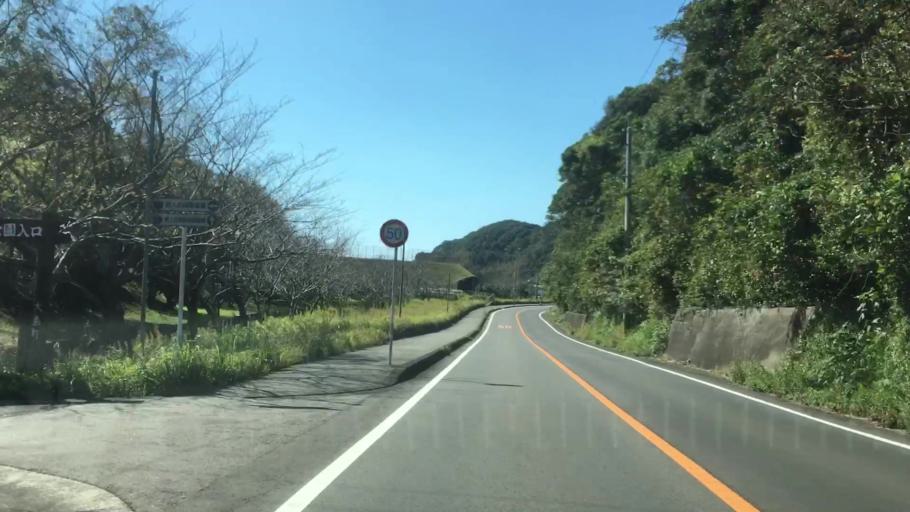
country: JP
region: Nagasaki
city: Sasebo
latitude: 33.0327
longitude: 129.6057
